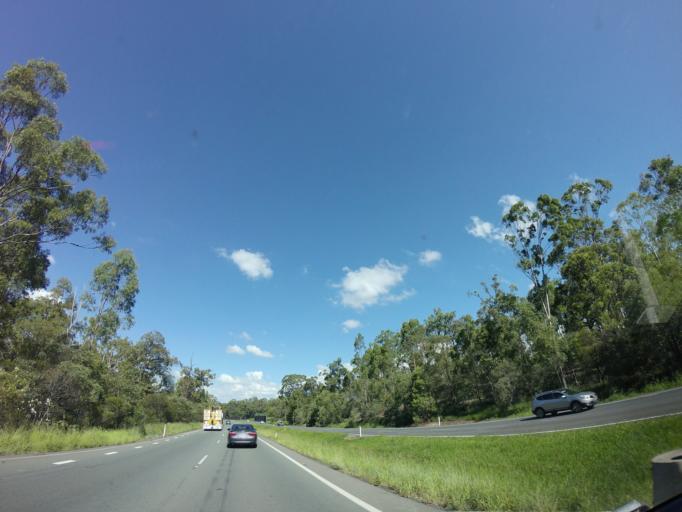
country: AU
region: Queensland
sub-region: Ipswich
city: Tivoli
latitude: -27.5816
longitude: 152.7583
